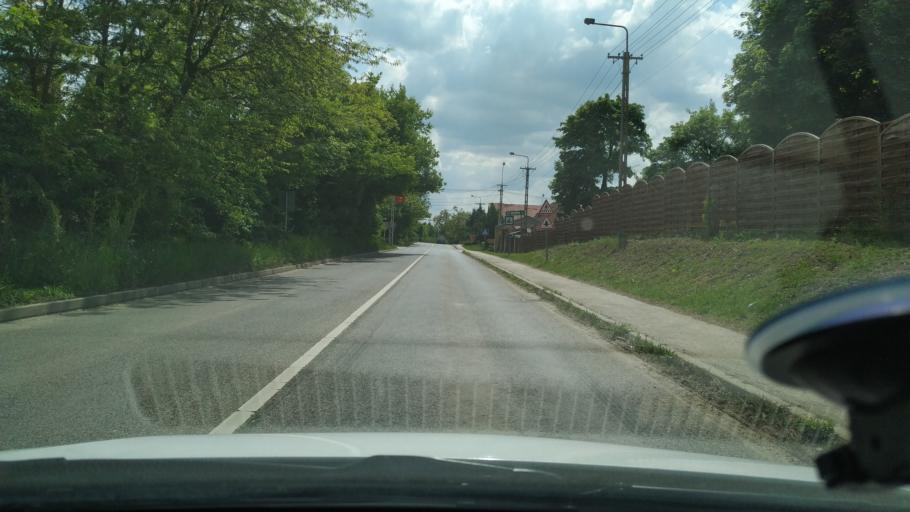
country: HU
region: Pest
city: Gyomro
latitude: 47.4177
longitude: 19.4073
